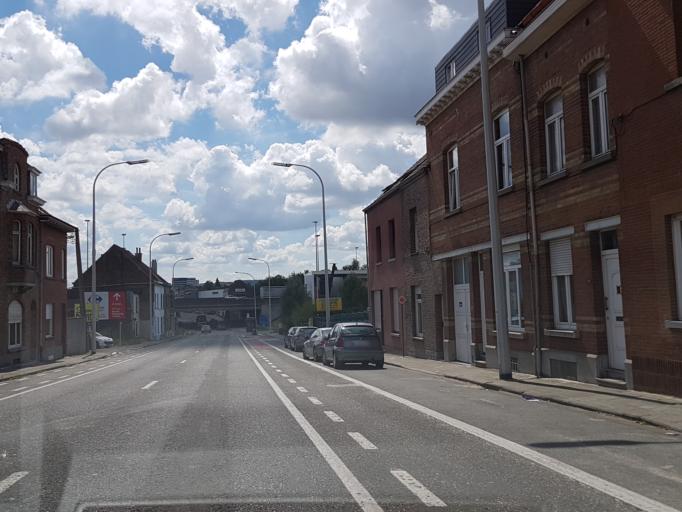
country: BE
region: Flanders
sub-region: Provincie Vlaams-Brabant
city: Dilbeek
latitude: 50.8811
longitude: 4.2783
